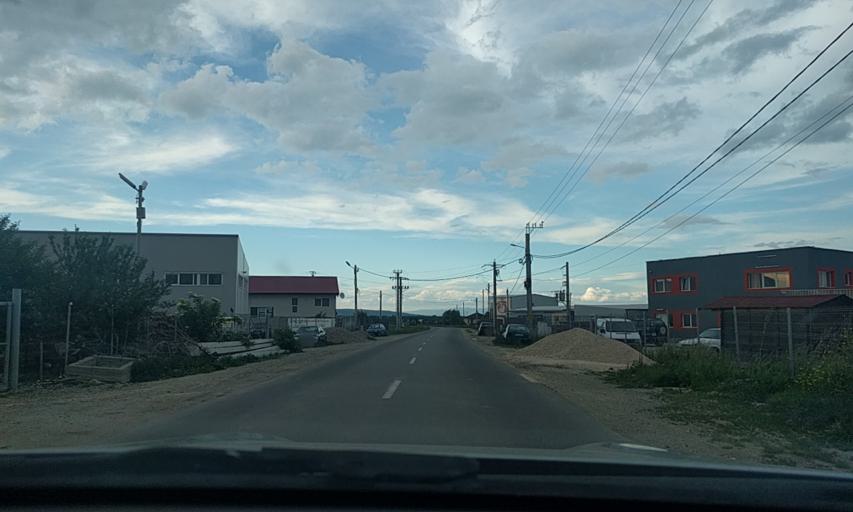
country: RO
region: Brasov
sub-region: Comuna Harman
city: Harman
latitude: 45.7241
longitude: 25.6976
